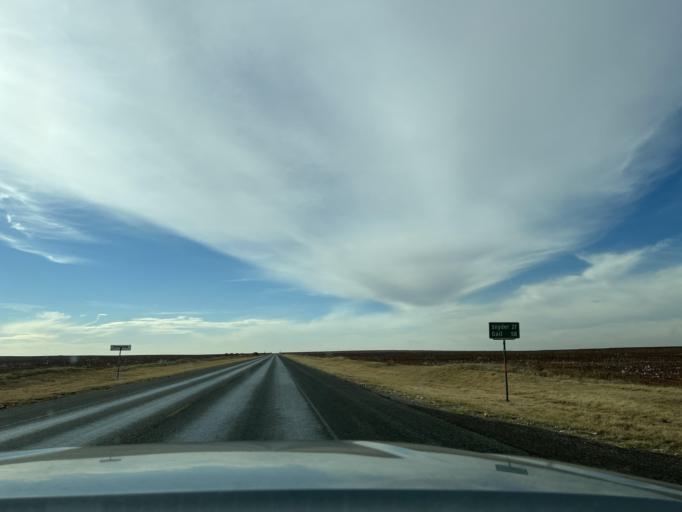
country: US
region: Texas
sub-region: Fisher County
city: Roby
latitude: 32.7419
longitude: -100.4404
